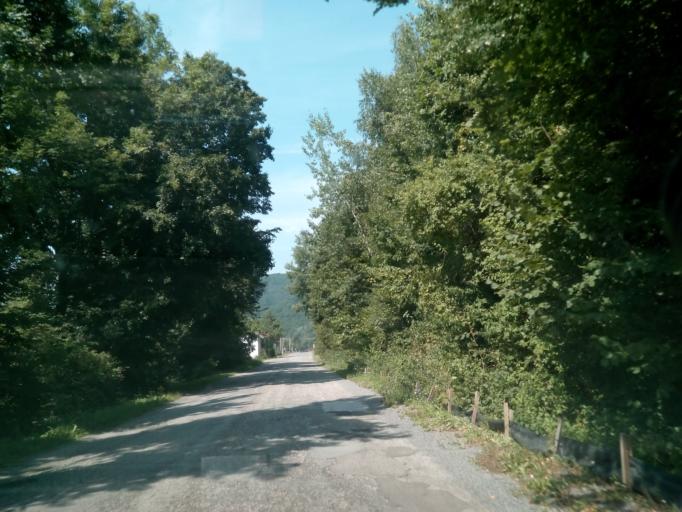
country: SK
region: Presovsky
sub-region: Okres Presov
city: Presov
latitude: 48.8768
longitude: 21.1370
